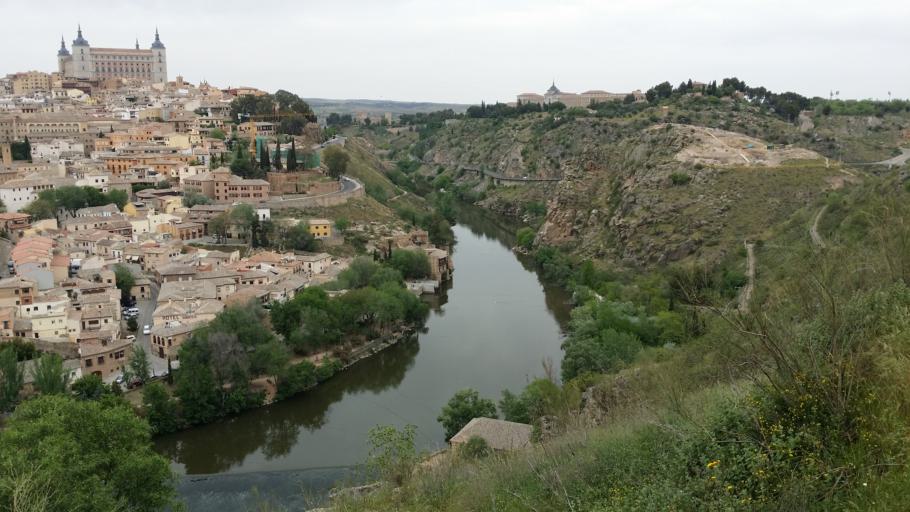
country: ES
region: Castille-La Mancha
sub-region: Province of Toledo
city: Toledo
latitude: 39.8503
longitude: -4.0229
